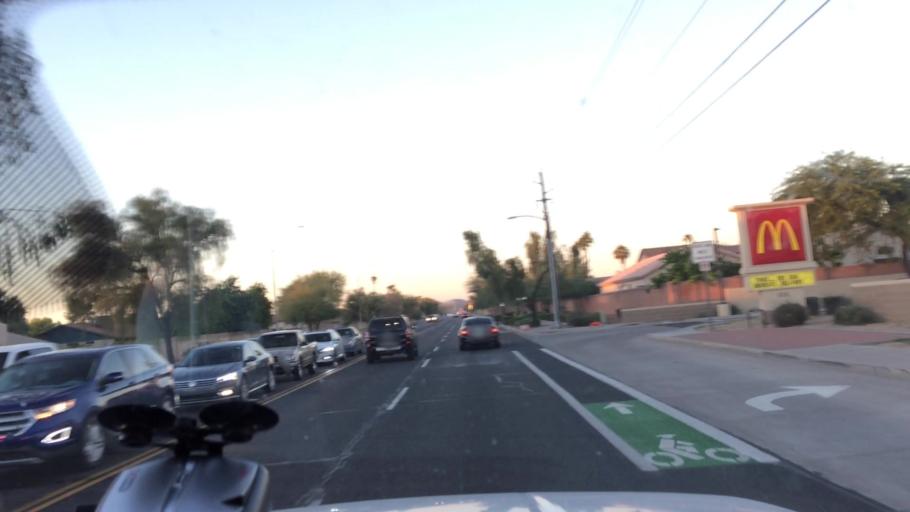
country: US
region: Arizona
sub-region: Maricopa County
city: Glendale
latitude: 33.6550
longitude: -112.0827
